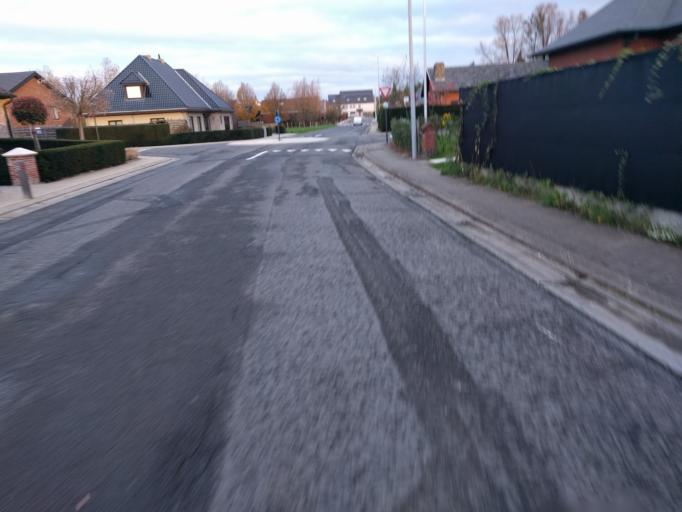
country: BE
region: Flanders
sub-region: Provincie West-Vlaanderen
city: Wevelgem
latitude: 50.8037
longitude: 3.1758
